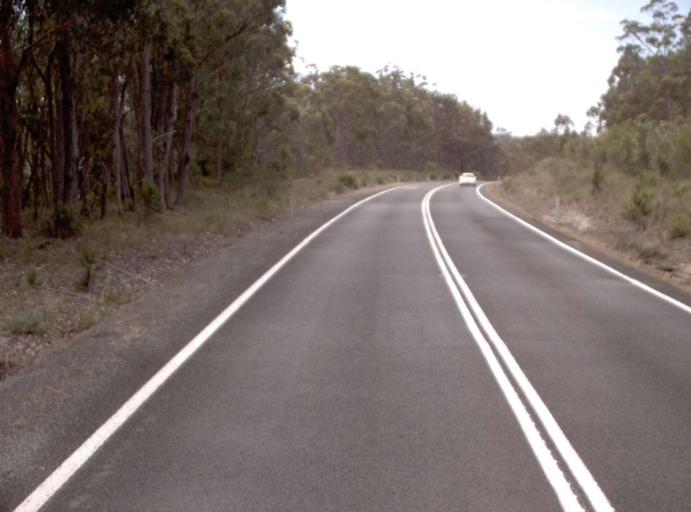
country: AU
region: New South Wales
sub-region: Bega Valley
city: Eden
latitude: -37.4860
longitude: 149.5503
